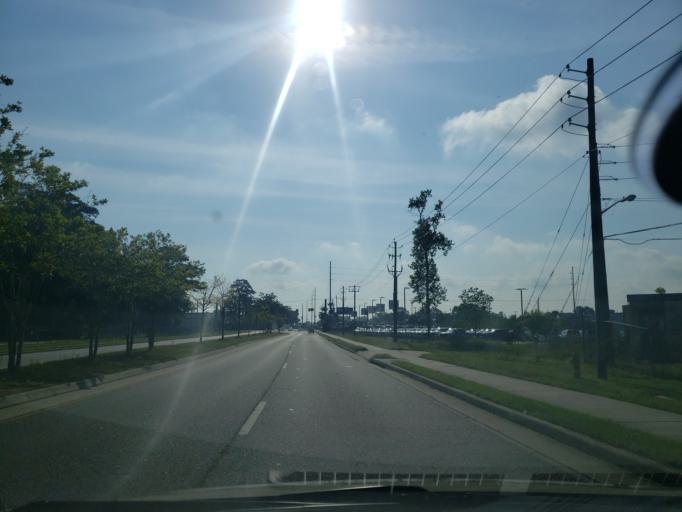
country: US
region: Georgia
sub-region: Chatham County
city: Montgomery
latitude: 32.0011
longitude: -81.1292
